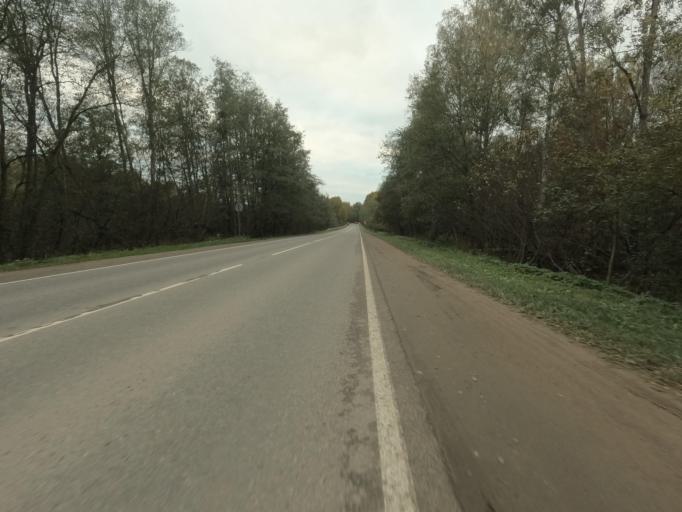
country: RU
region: Leningrad
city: Pavlovo
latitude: 59.7952
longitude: 30.9514
